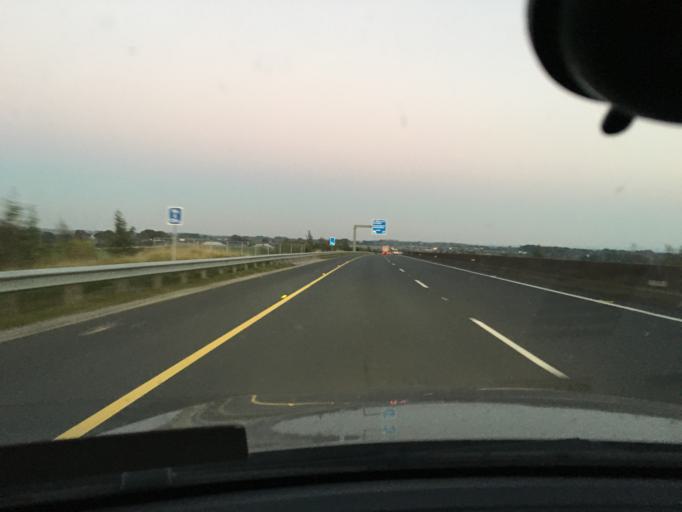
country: IE
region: Connaught
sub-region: County Galway
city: Athenry
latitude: 53.2915
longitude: -8.7706
